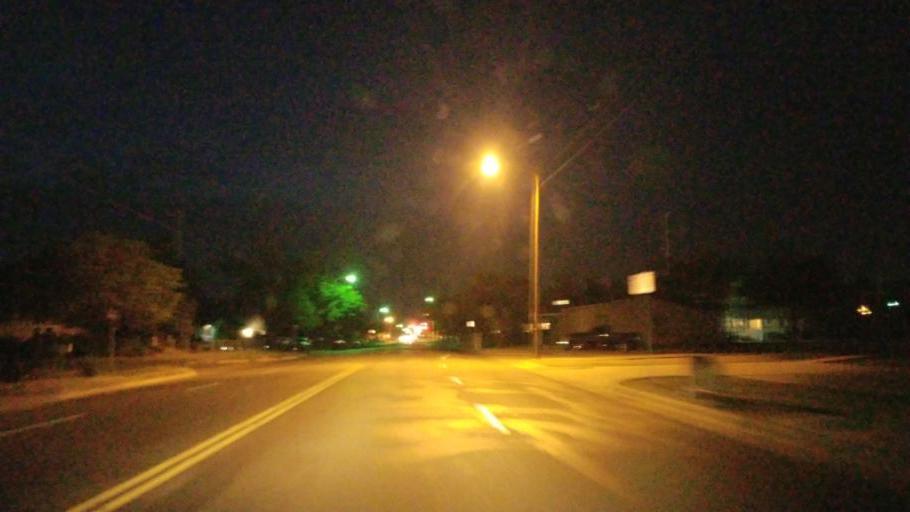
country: US
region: Texas
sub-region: Potter County
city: Amarillo
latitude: 35.1984
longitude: -101.8260
